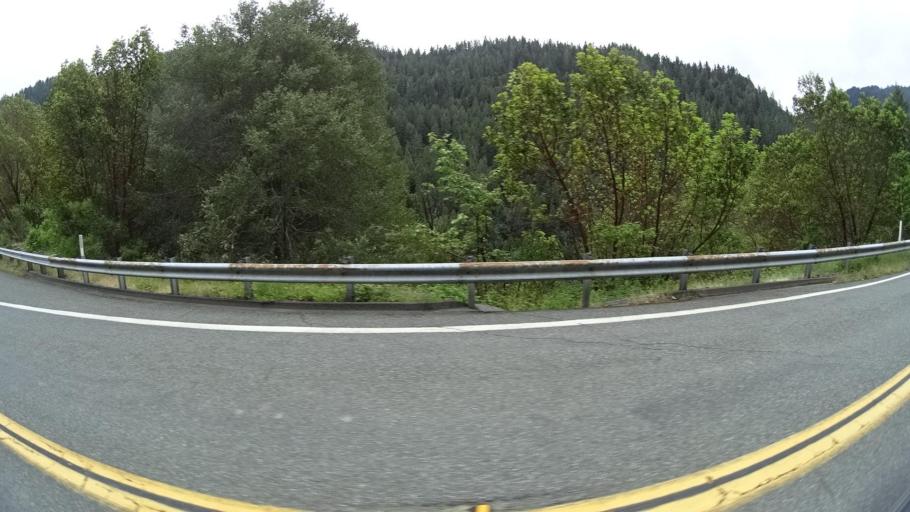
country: US
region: California
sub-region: Humboldt County
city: Willow Creek
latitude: 41.2779
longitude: -123.5926
